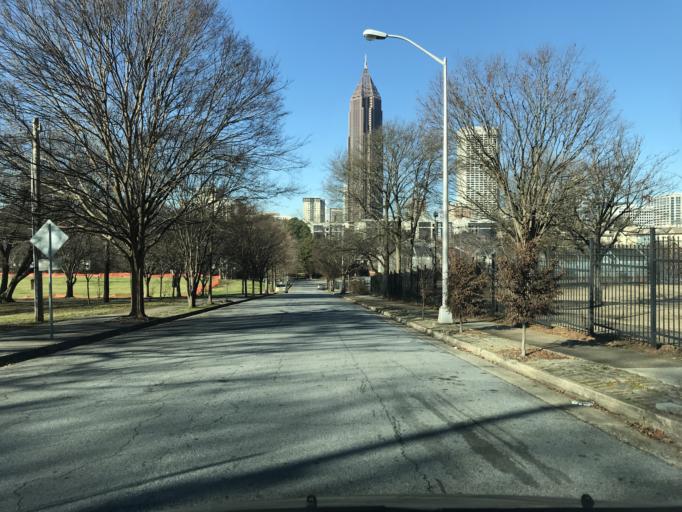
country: US
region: Georgia
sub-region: Fulton County
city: Atlanta
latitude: 33.7699
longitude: -84.3757
